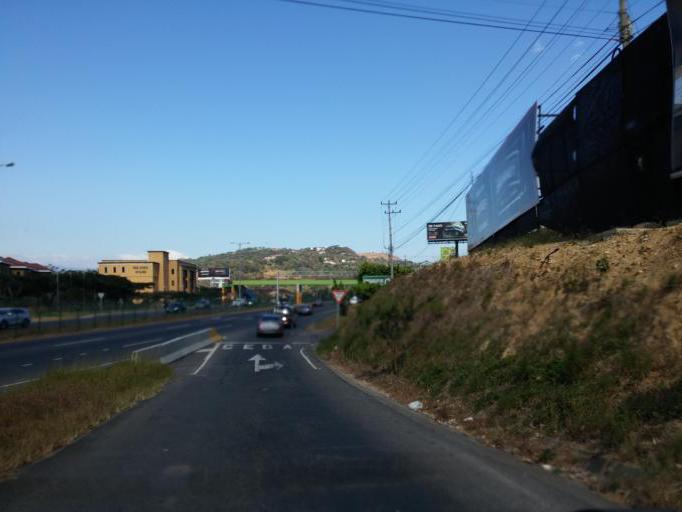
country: CR
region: San Jose
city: Santa Ana
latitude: 9.9432
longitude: -84.1937
